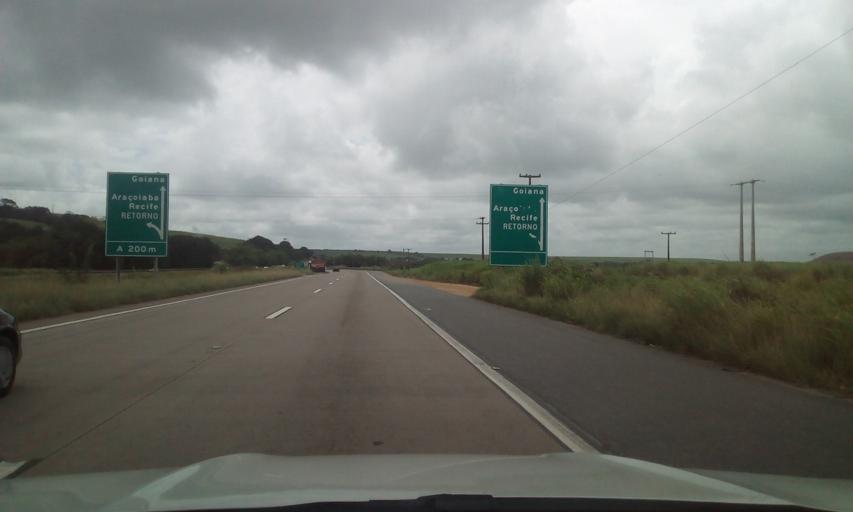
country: BR
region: Pernambuco
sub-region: Itapissuma
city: Itapissuma
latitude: -7.7620
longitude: -34.9353
